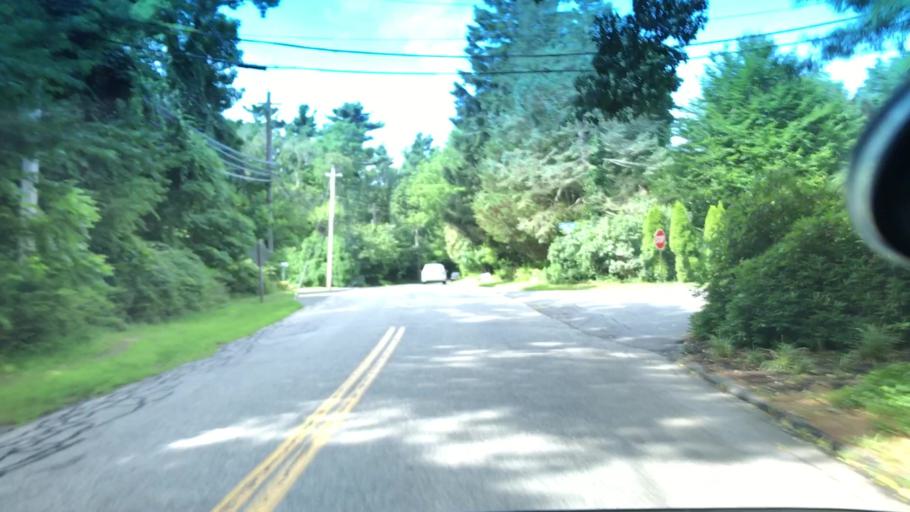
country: US
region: New York
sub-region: Suffolk County
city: Wading River
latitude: 40.9632
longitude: -72.8269
